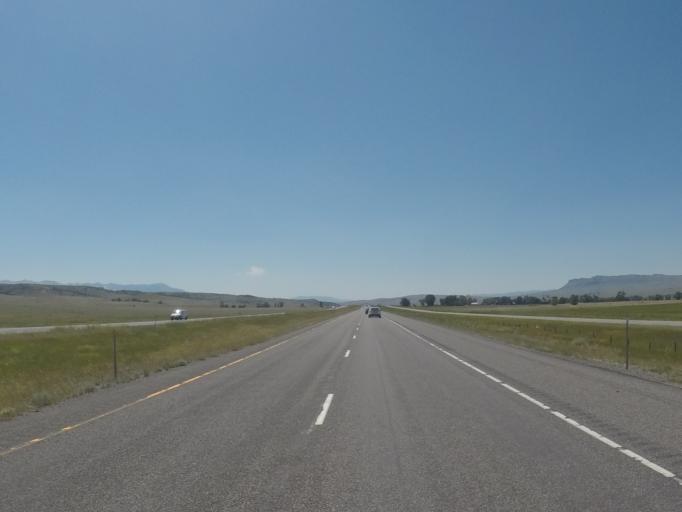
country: US
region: Montana
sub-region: Sweet Grass County
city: Big Timber
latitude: 45.7543
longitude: -110.1438
